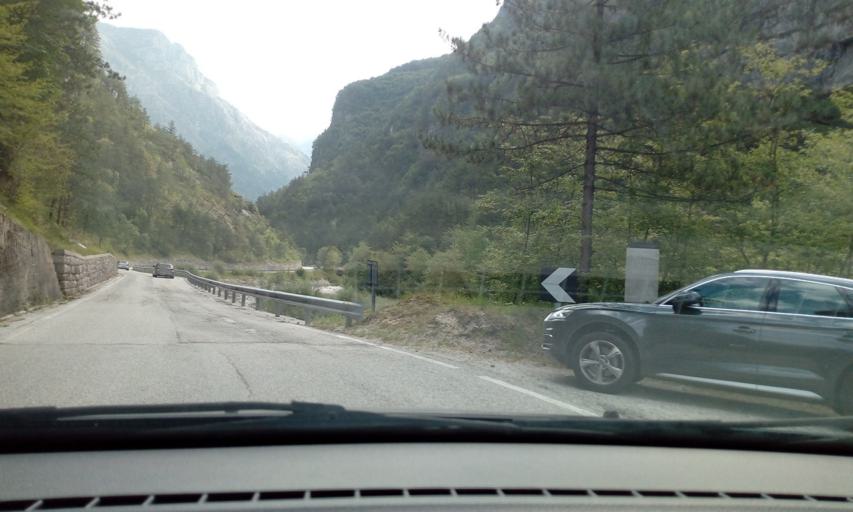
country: IT
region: Friuli Venezia Giulia
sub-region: Provincia di Udine
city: Chiusaforte
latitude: 46.3960
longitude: 13.3418
